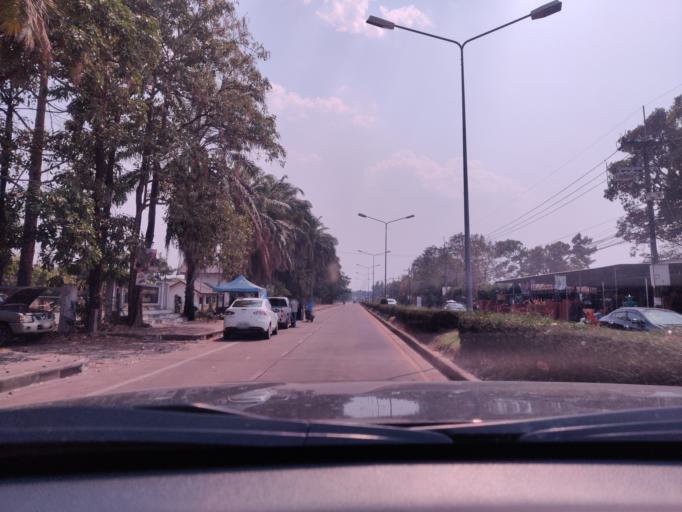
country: TH
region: Sisaket
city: Si Sa Ket
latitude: 15.1055
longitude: 104.3155
